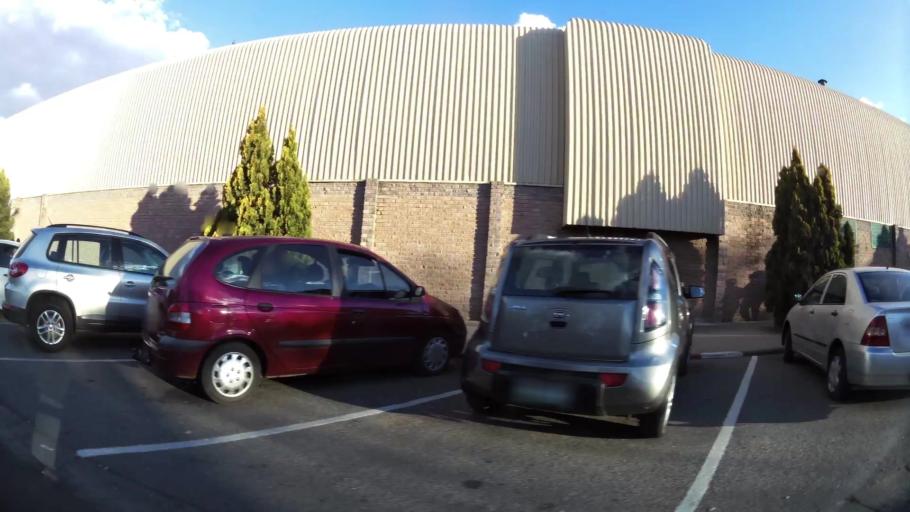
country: ZA
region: North-West
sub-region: Dr Kenneth Kaunda District Municipality
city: Potchefstroom
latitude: -26.7308
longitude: 27.0942
